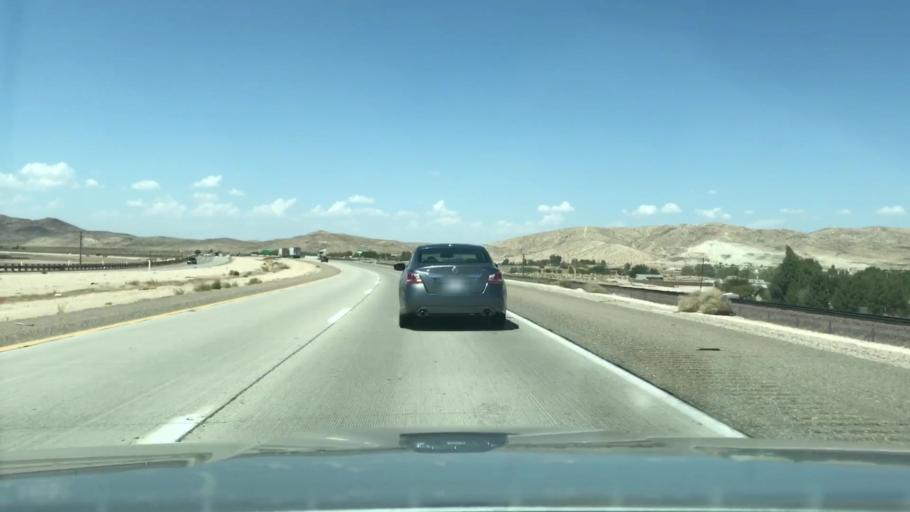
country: US
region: California
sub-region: San Bernardino County
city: Lenwood
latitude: 34.9037
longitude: -117.0933
